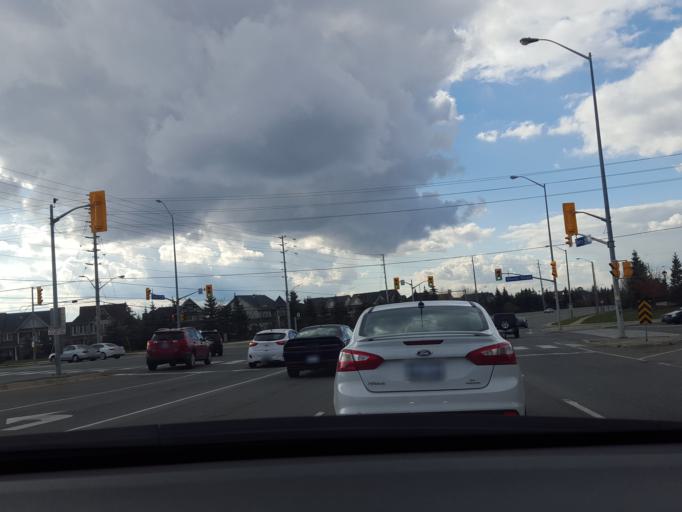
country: CA
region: Ontario
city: Brampton
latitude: 43.6330
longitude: -79.7219
